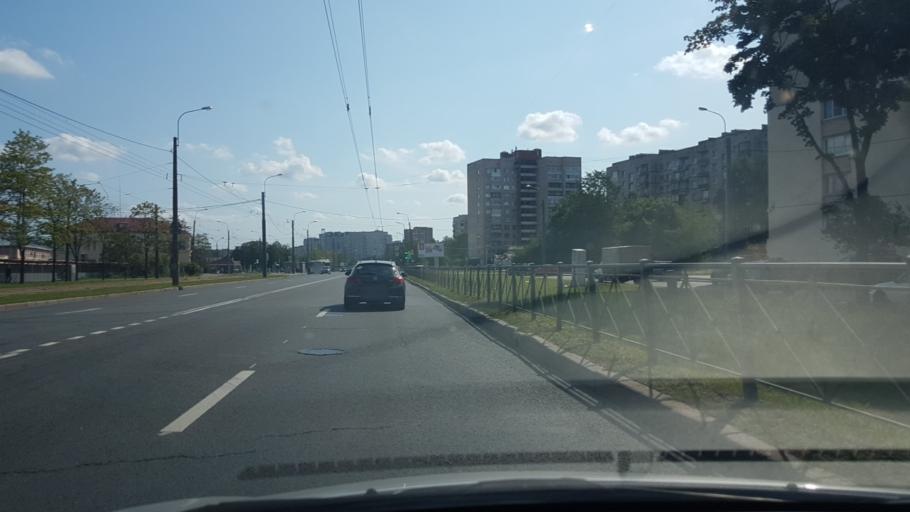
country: RU
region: St.-Petersburg
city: Sosnovaya Polyana
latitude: 59.8350
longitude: 30.1532
